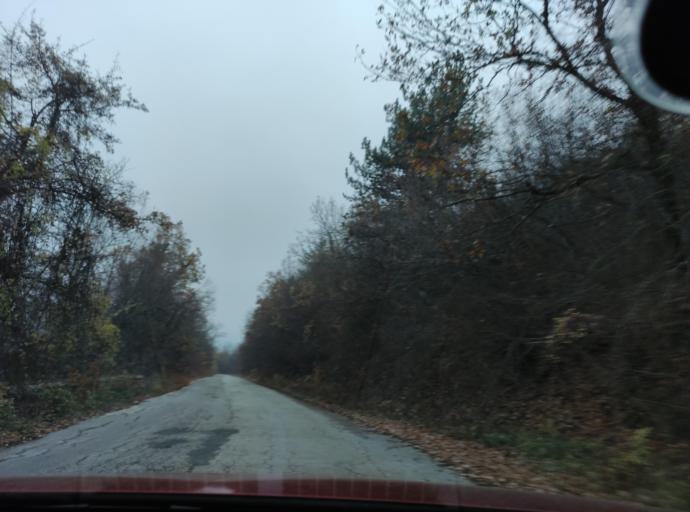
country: BG
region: Lovech
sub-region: Obshtina Yablanitsa
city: Yablanitsa
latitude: 43.1024
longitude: 24.0711
